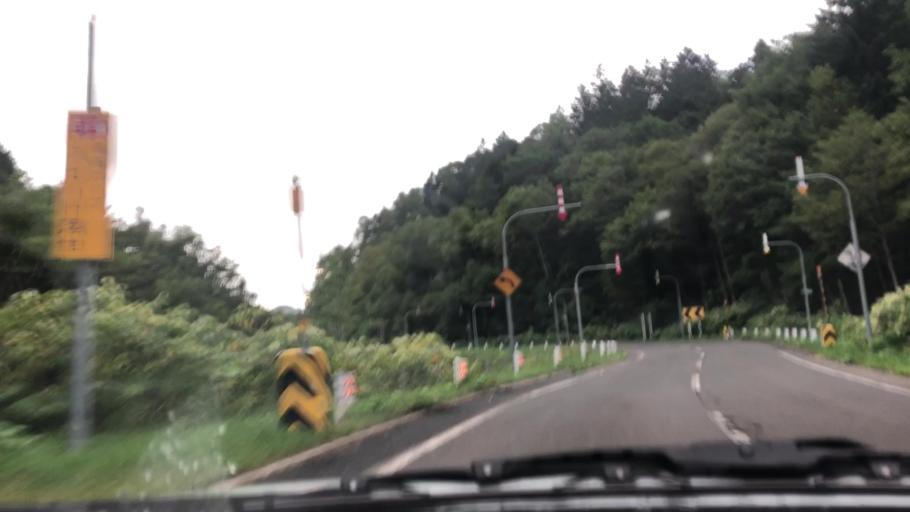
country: JP
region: Hokkaido
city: Shimo-furano
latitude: 42.9328
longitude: 142.3740
